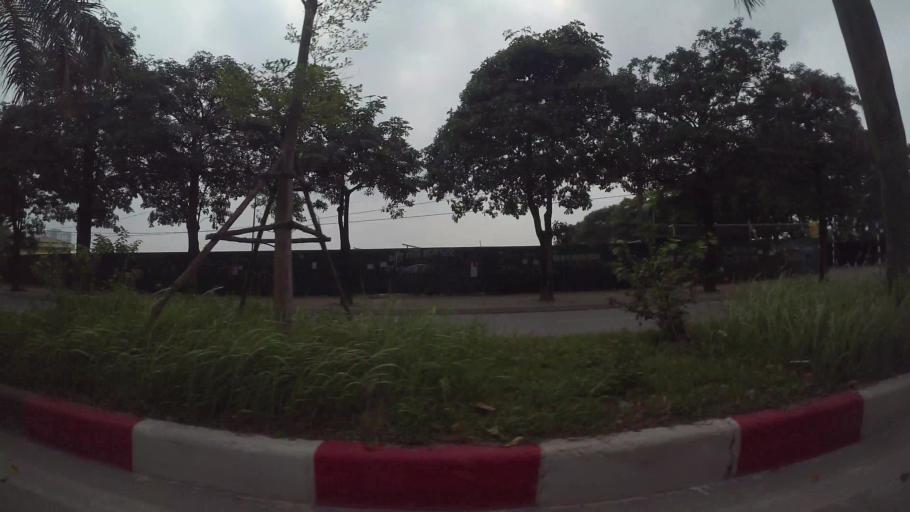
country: VN
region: Ha Noi
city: Trau Quy
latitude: 21.0635
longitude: 105.9083
